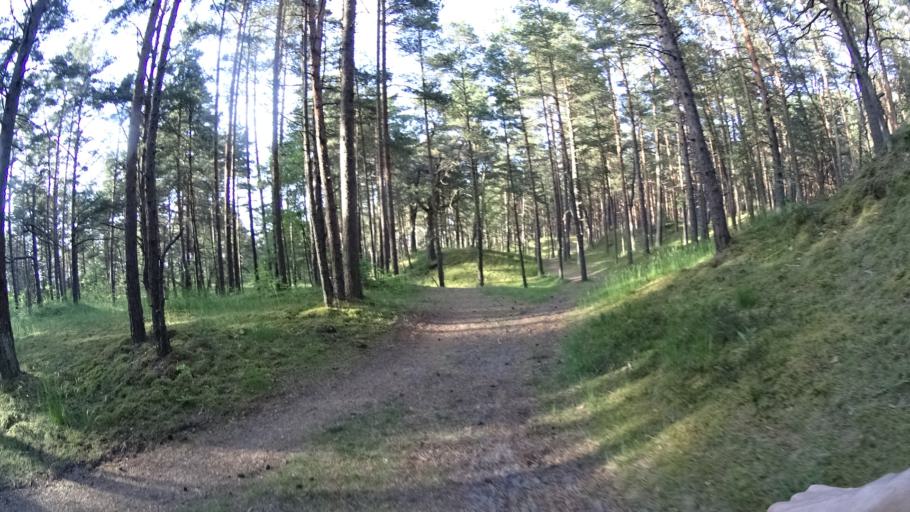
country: LV
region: Riga
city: Jaunciems
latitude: 57.0825
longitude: 24.1159
